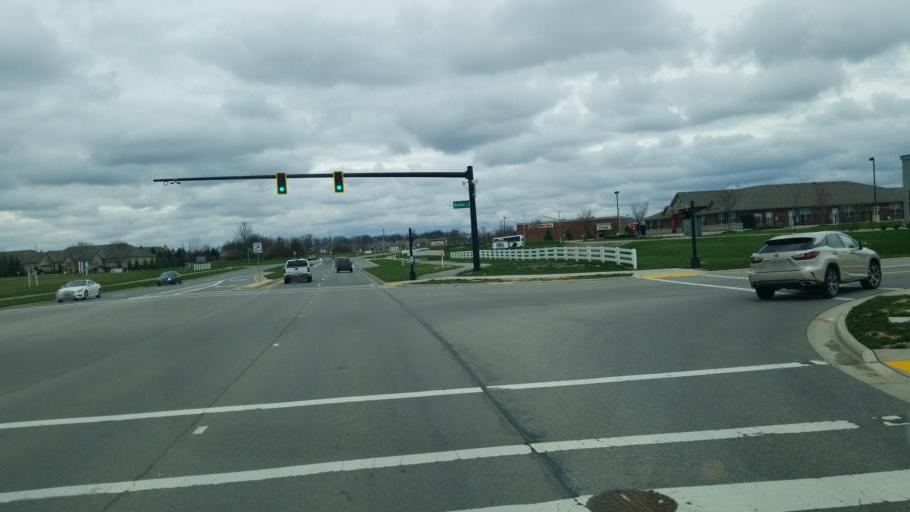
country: US
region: Ohio
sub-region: Delaware County
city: Powell
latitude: 40.1667
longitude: -83.0885
